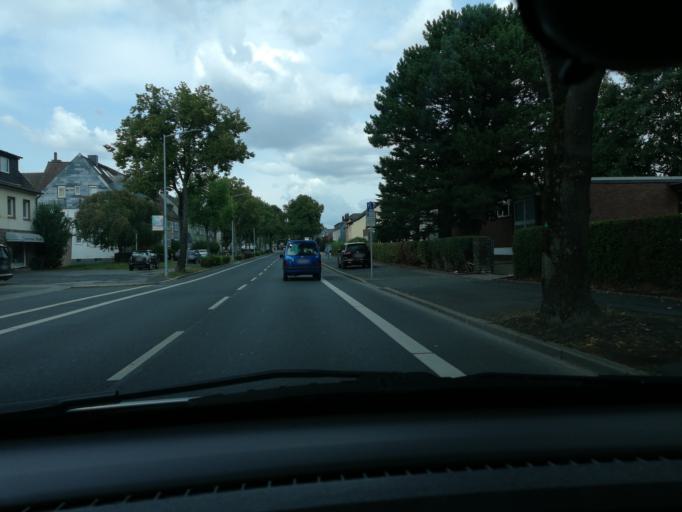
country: DE
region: North Rhine-Westphalia
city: Witten
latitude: 51.4204
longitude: 7.2762
